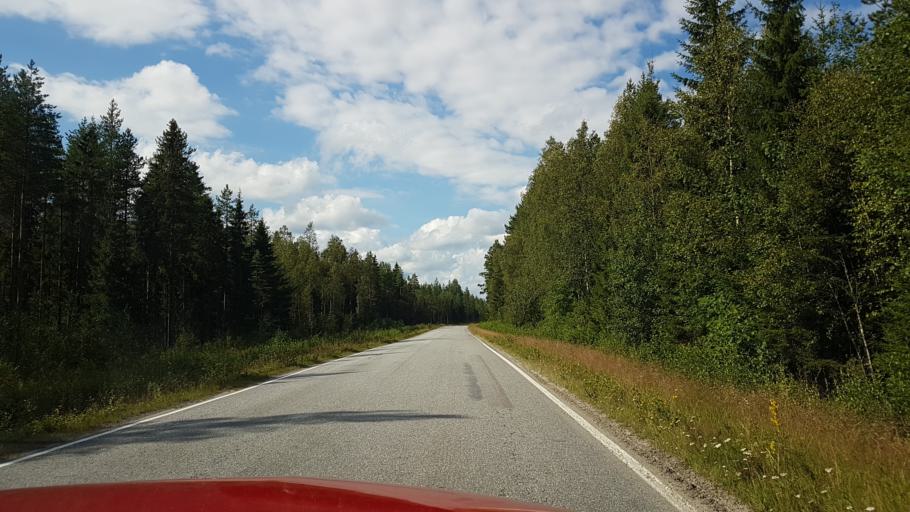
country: FI
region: Northern Ostrobothnia
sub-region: Ylivieska
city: Himanka
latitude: 64.0815
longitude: 23.7282
